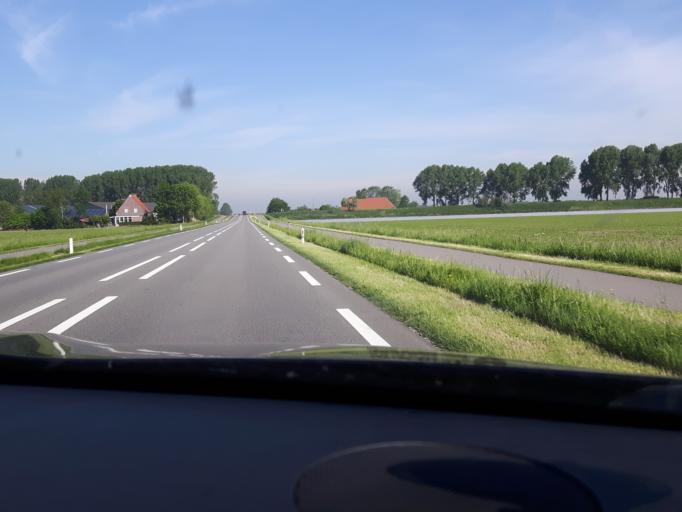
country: NL
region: North Brabant
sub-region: Gemeente Steenbergen
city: Steenbergen
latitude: 51.5963
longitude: 4.2830
